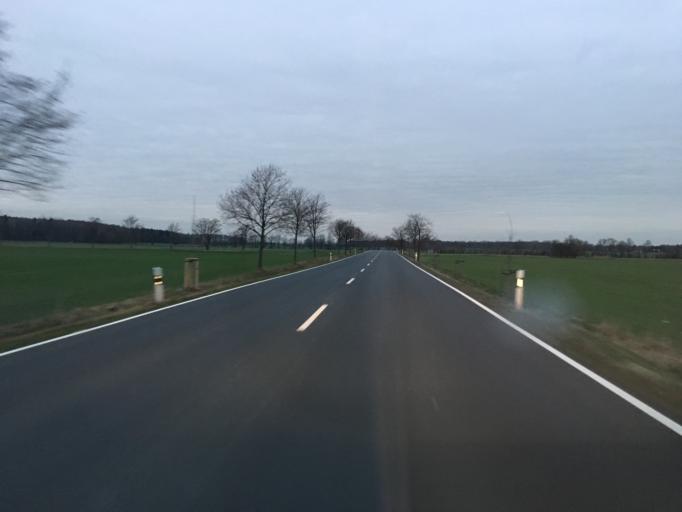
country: DE
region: Saxony
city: Oschatz
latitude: 51.3194
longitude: 13.0624
